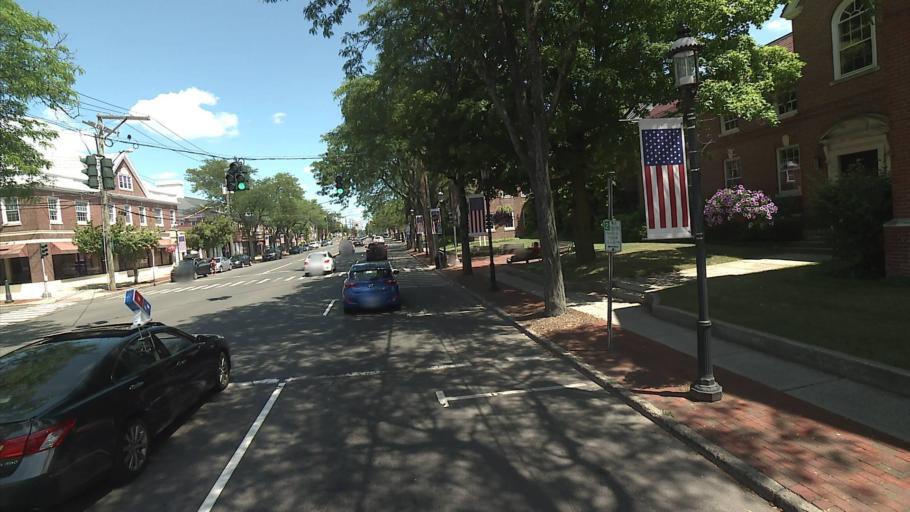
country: US
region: Connecticut
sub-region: Fairfield County
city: Fairfield
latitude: 41.1419
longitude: -73.2559
